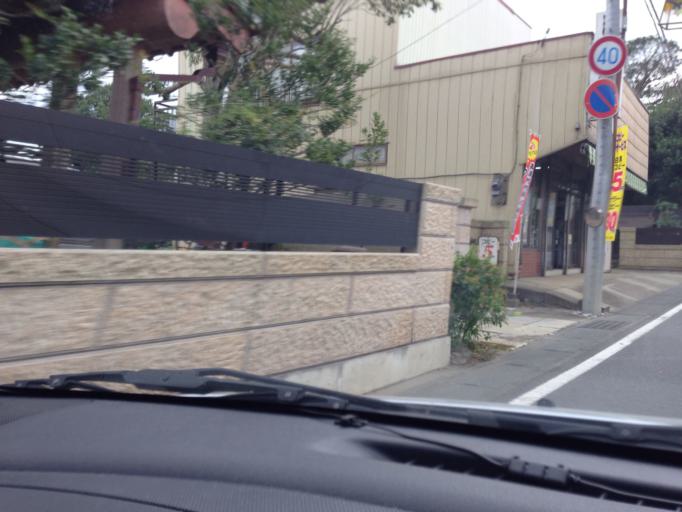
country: JP
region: Ibaraki
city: Inashiki
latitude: 36.0221
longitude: 140.2939
